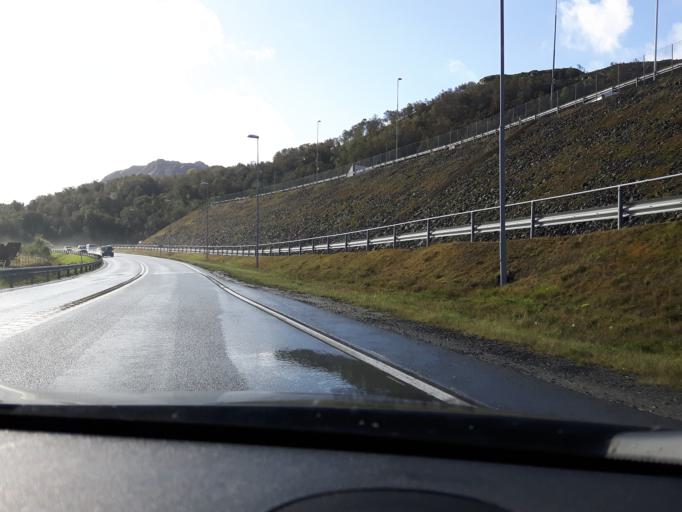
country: NO
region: Rogaland
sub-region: Gjesdal
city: Algard
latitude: 58.7442
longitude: 5.9306
